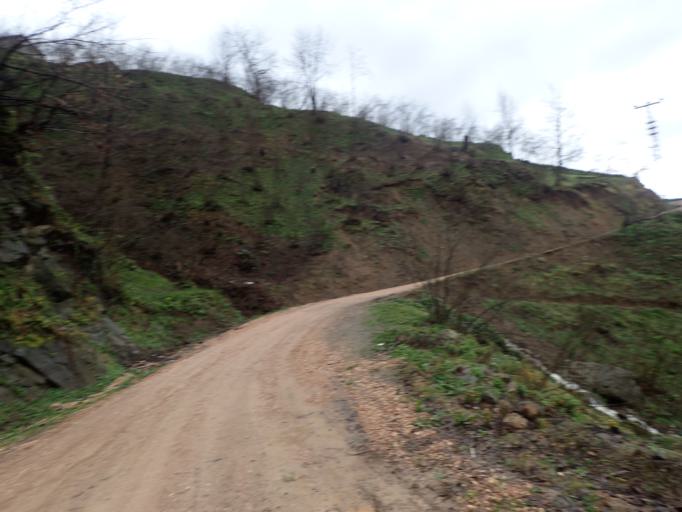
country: TR
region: Ordu
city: Camas
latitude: 40.8697
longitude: 37.5036
